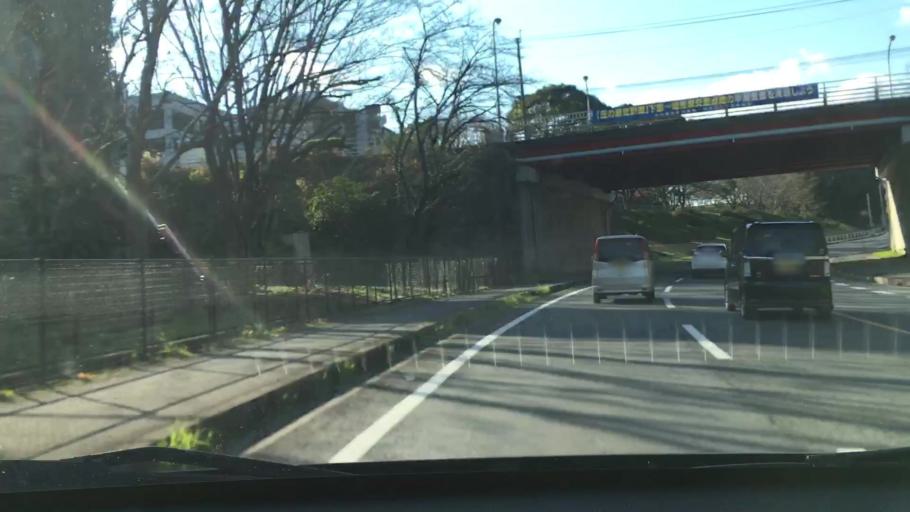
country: JP
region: Oita
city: Oita
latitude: 33.2251
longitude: 131.6525
